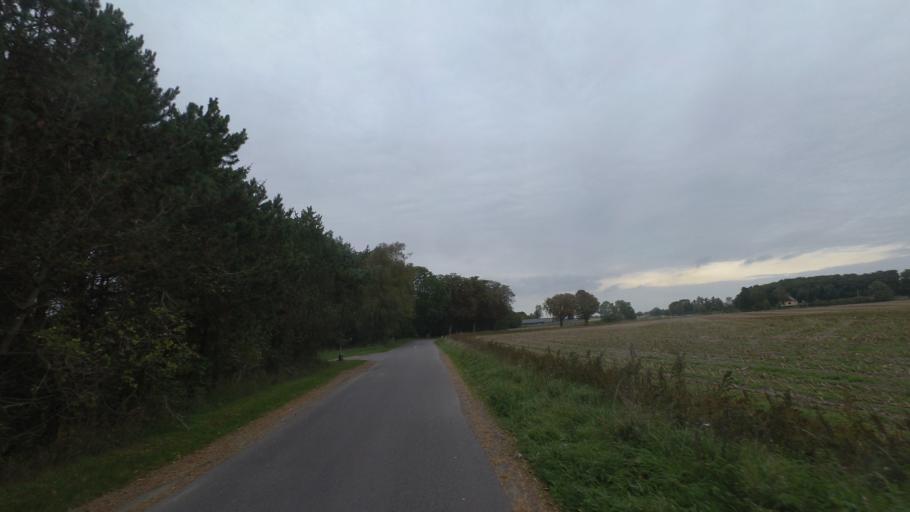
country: DK
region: Capital Region
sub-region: Bornholm Kommune
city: Akirkeby
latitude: 55.0063
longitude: 14.9919
